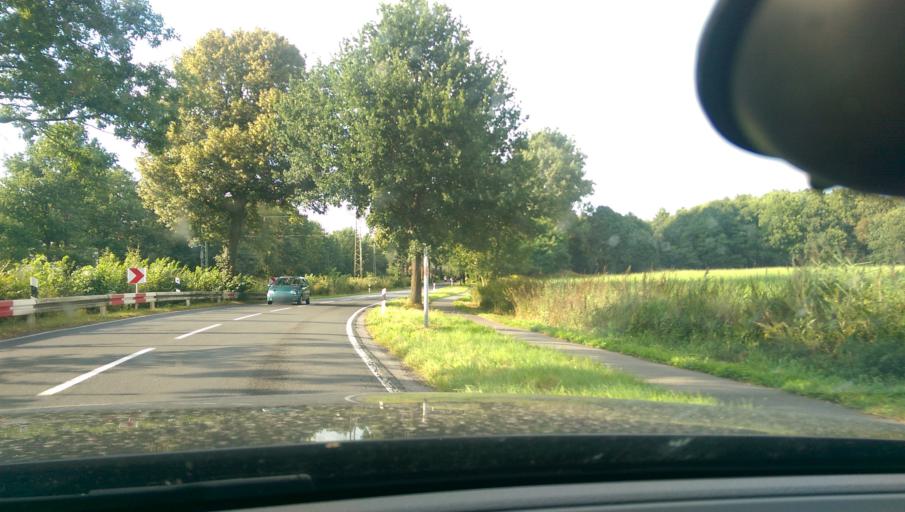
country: DE
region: Lower Saxony
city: Neustadt am Rubenberge
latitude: 52.4739
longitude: 9.4545
